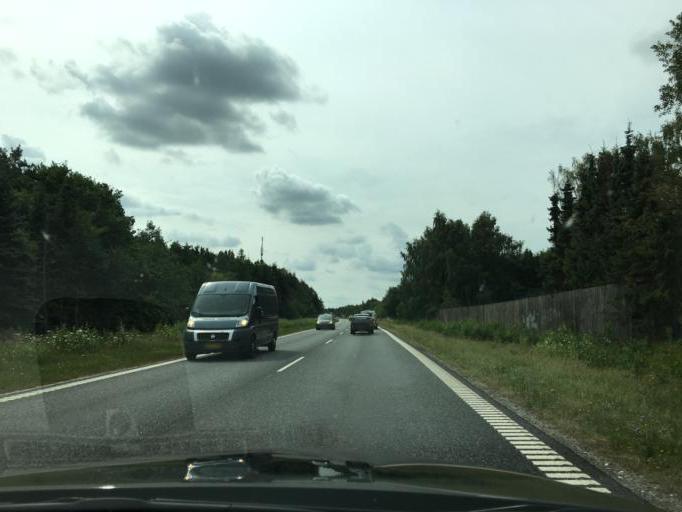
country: DK
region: Capital Region
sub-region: Hillerod Kommune
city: Hillerod
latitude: 55.9440
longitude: 12.2445
